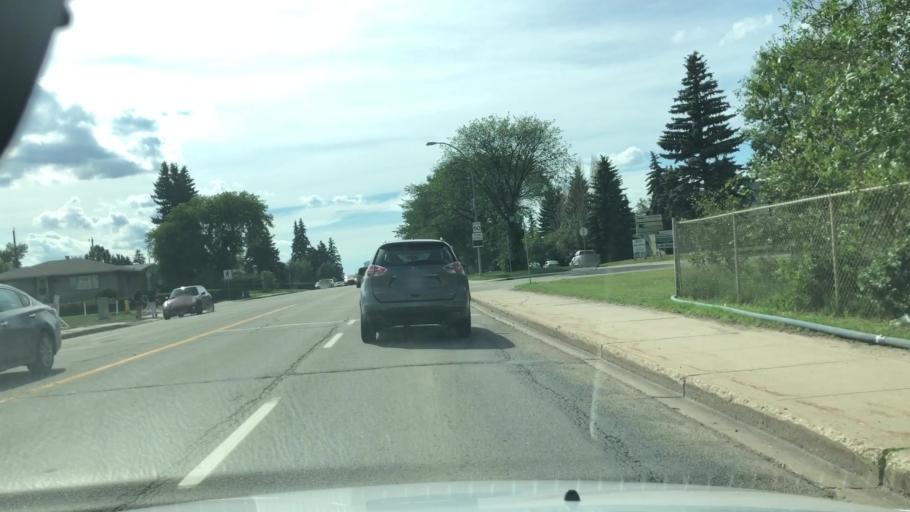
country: CA
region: Alberta
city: Edmonton
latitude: 53.5404
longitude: -113.4302
